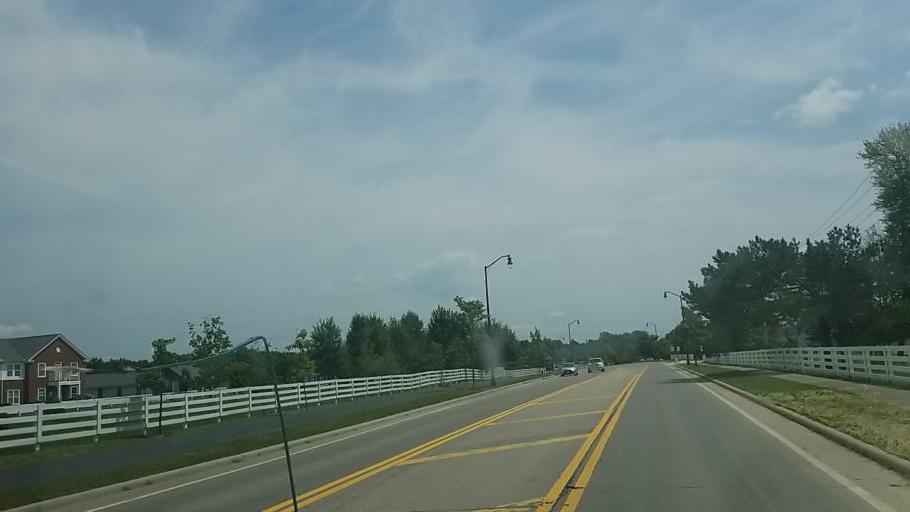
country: US
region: Ohio
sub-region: Franklin County
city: New Albany
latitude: 40.0545
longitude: -82.8462
